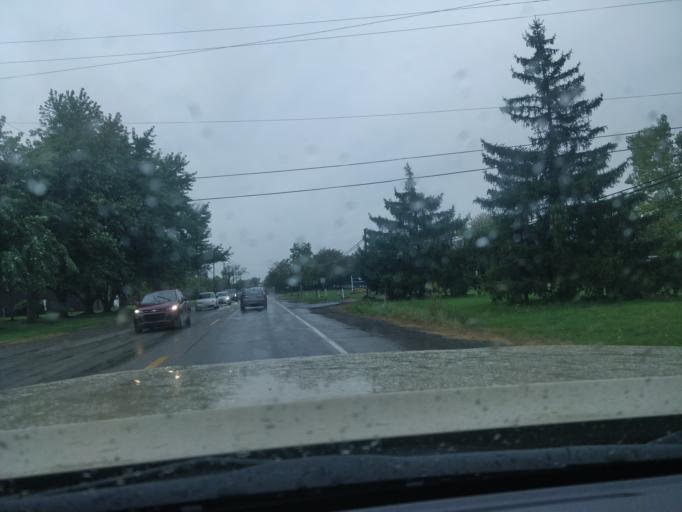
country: US
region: Michigan
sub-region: Wayne County
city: Woodhaven
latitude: 42.1264
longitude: -83.2183
